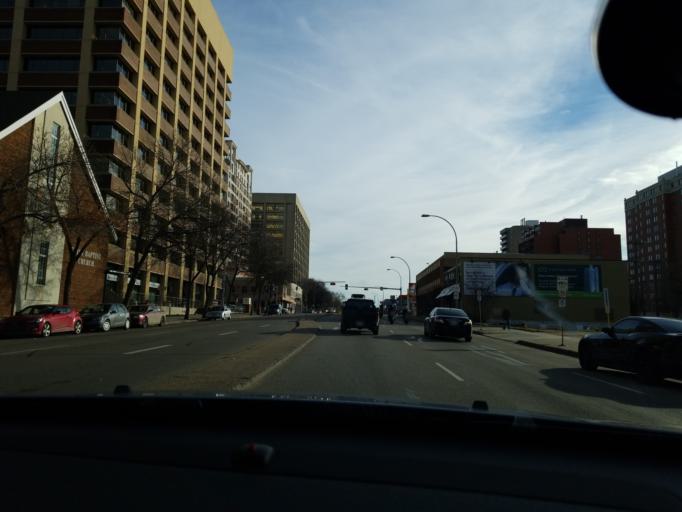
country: CA
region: Alberta
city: Edmonton
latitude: 53.5399
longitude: -113.5085
